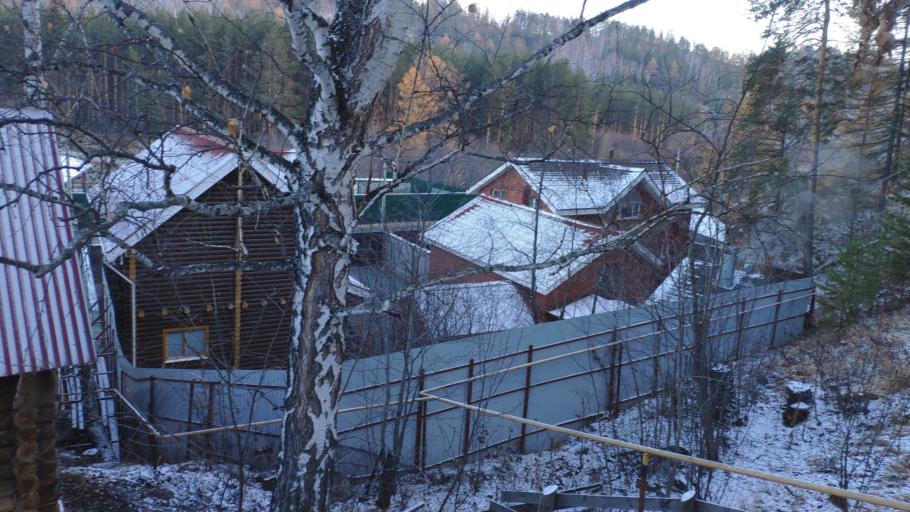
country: RU
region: Bashkortostan
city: Abzakovo
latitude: 53.8055
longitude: 58.6338
